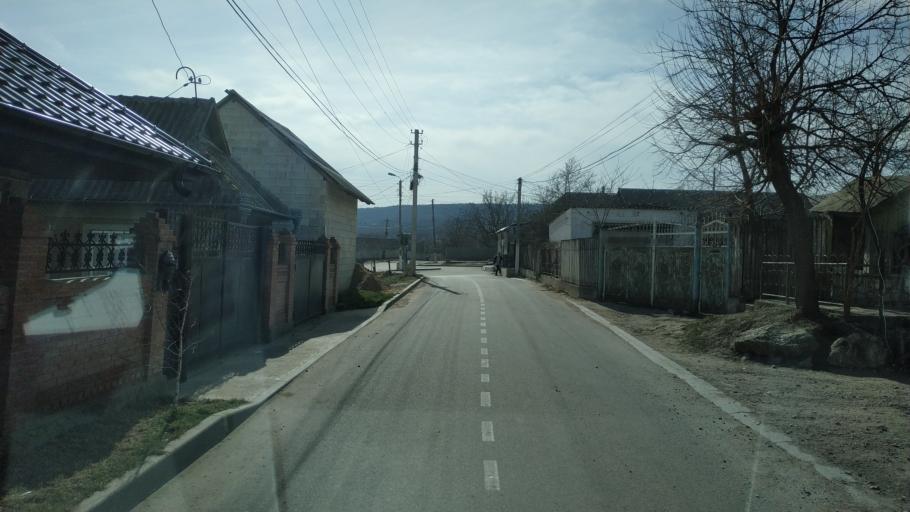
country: MD
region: Straseni
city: Straseni
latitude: 47.0944
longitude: 28.6513
